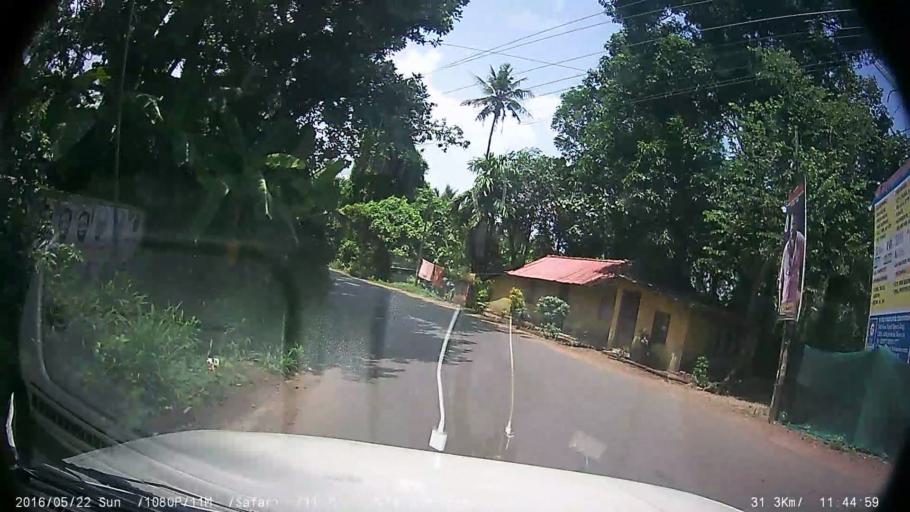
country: IN
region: Kerala
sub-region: Kottayam
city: Kottayam
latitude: 9.5416
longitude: 76.5198
